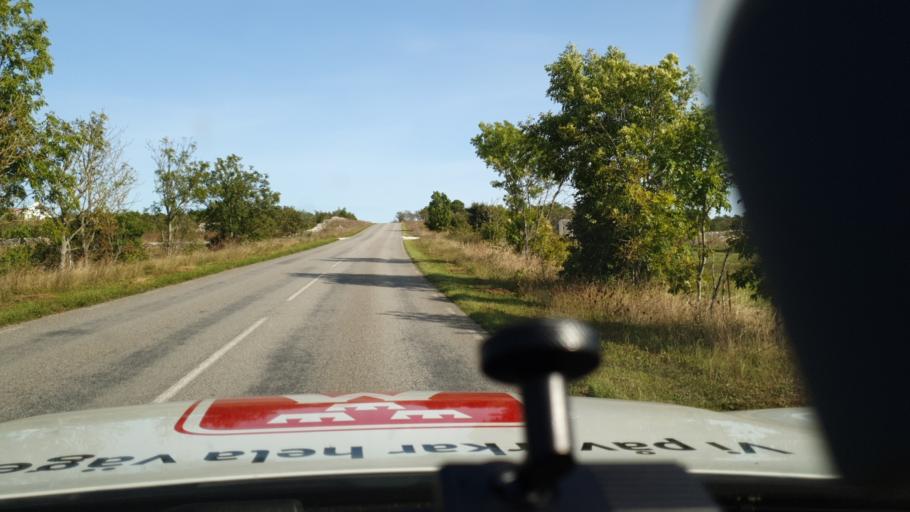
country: SE
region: Gotland
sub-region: Gotland
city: Slite
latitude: 57.9274
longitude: 19.1466
